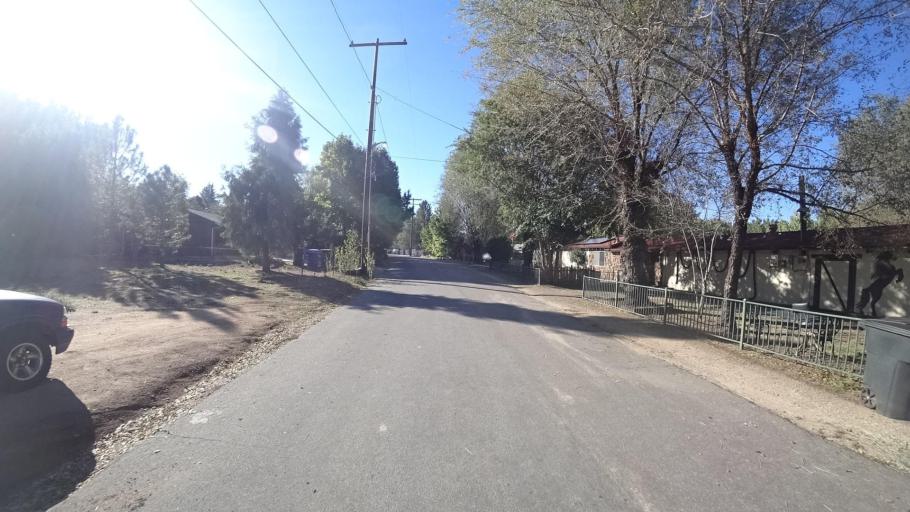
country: US
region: California
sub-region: San Diego County
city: Pine Valley
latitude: 32.8312
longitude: -116.5289
